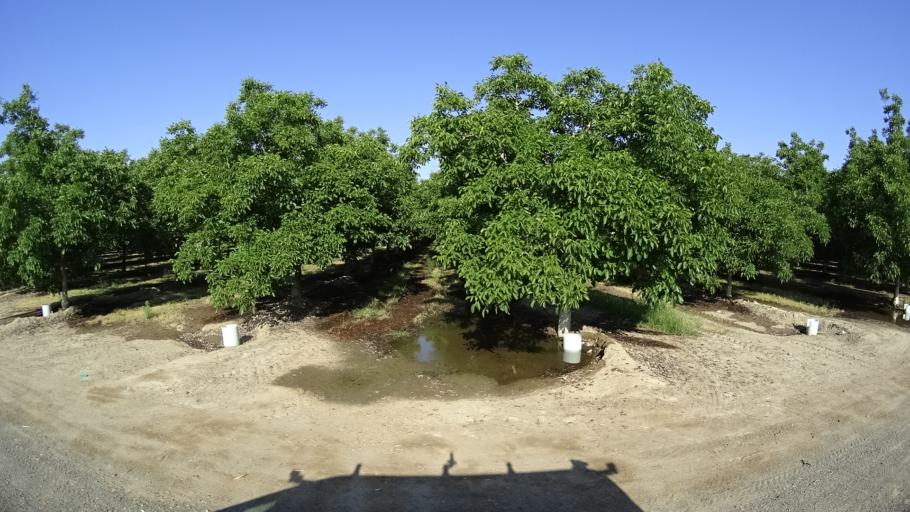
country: US
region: California
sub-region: Kings County
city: Home Garden
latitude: 36.2739
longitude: -119.5652
